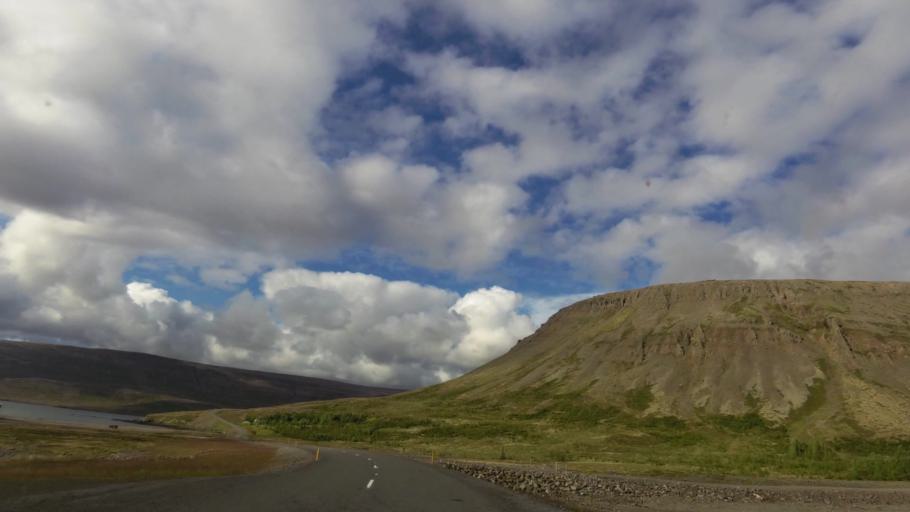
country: IS
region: West
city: Olafsvik
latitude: 65.5146
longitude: -23.8354
